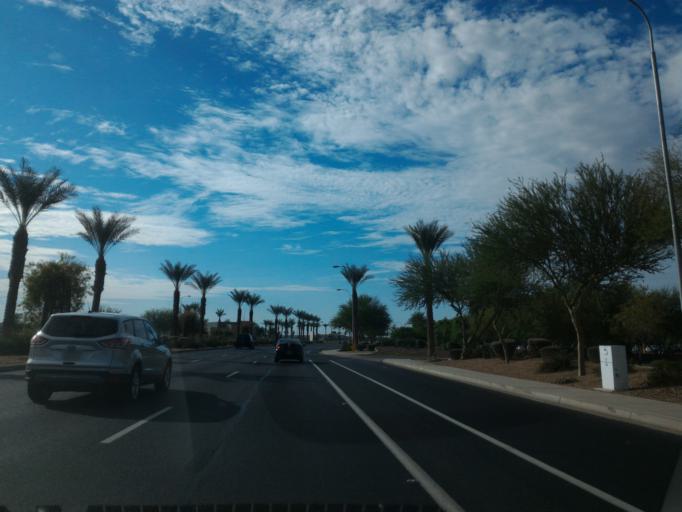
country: US
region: Arizona
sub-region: Maricopa County
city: Chandler
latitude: 33.2898
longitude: -111.8919
